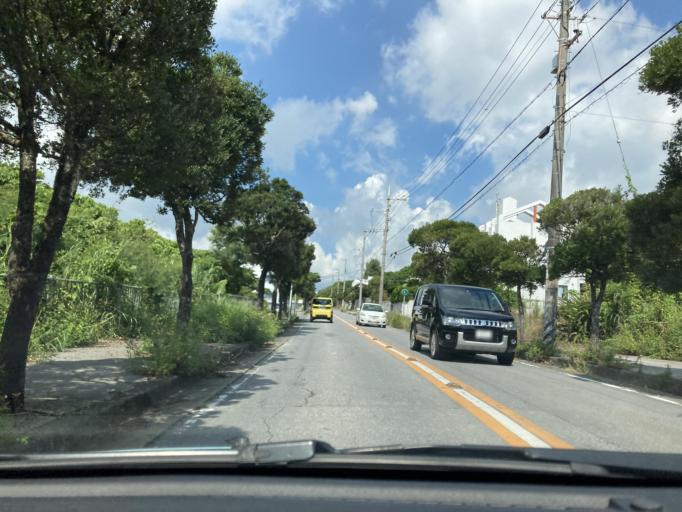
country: JP
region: Okinawa
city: Tomigusuku
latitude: 26.1468
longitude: 127.7634
